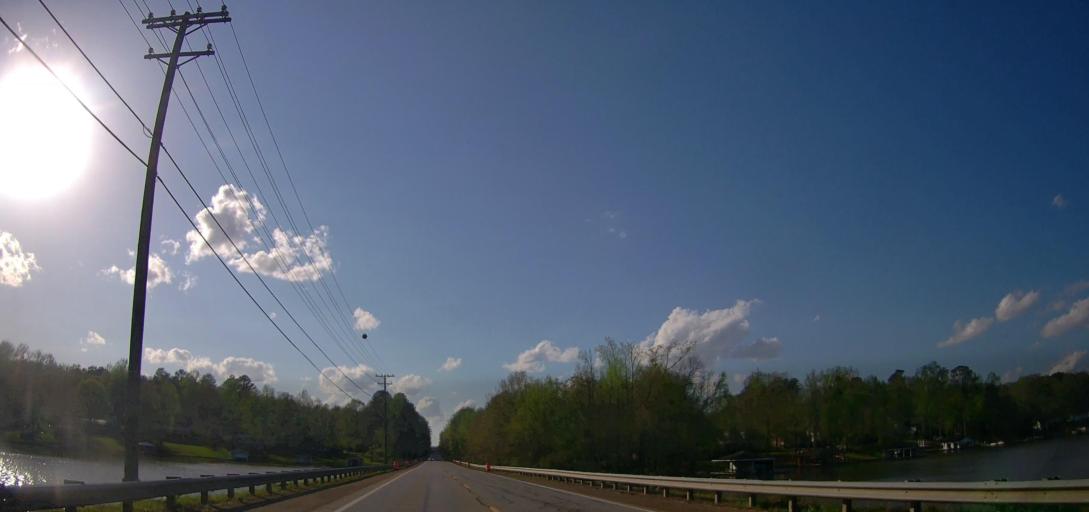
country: US
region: Georgia
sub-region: Putnam County
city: Eatonton
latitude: 33.1634
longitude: -83.3751
